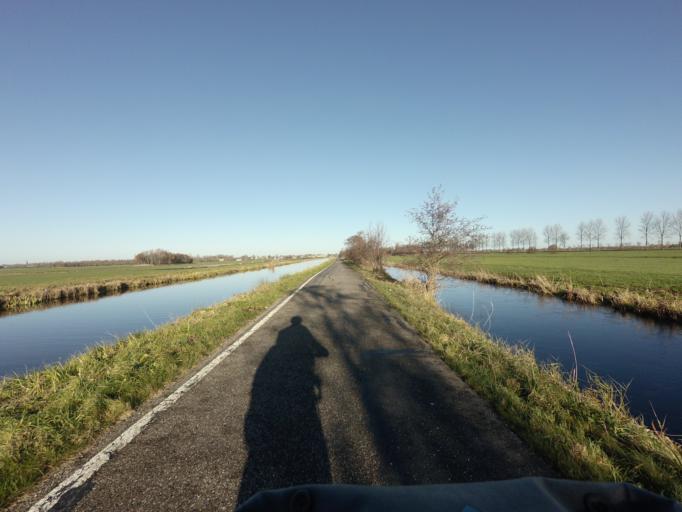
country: NL
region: Utrecht
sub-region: Gemeente De Ronde Venen
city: Mijdrecht
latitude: 52.1838
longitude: 4.9051
